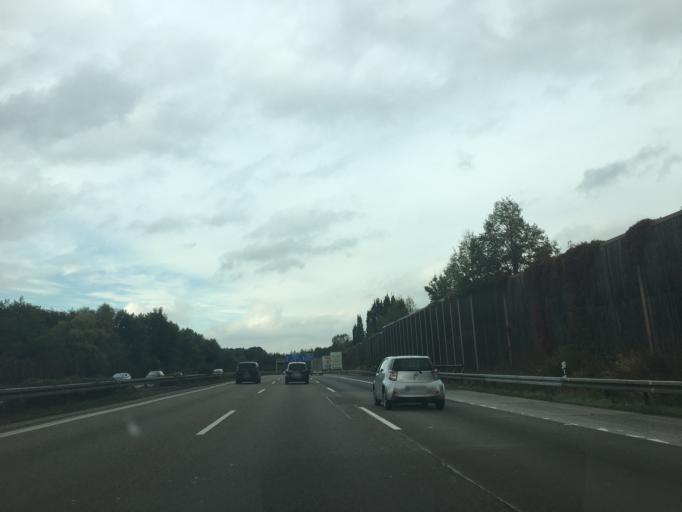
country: DE
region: North Rhine-Westphalia
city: Leichlingen
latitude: 51.1011
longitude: 6.9882
